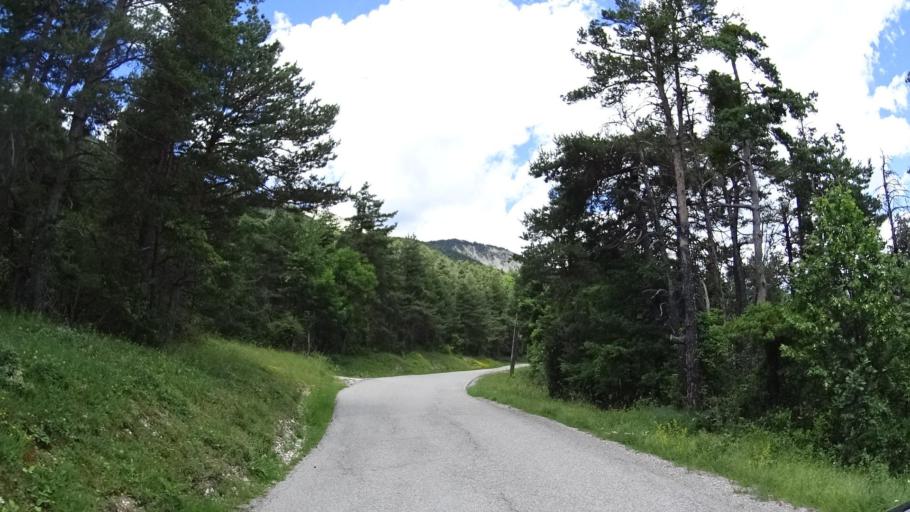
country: FR
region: Provence-Alpes-Cote d'Azur
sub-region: Departement des Alpes-de-Haute-Provence
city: Annot
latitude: 44.0147
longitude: 6.6279
